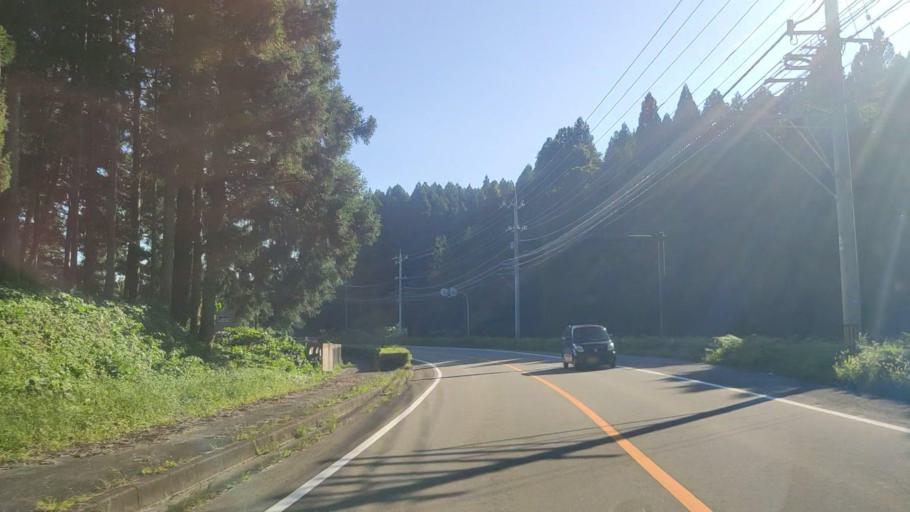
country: JP
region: Ishikawa
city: Nanao
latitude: 37.1203
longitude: 136.8619
